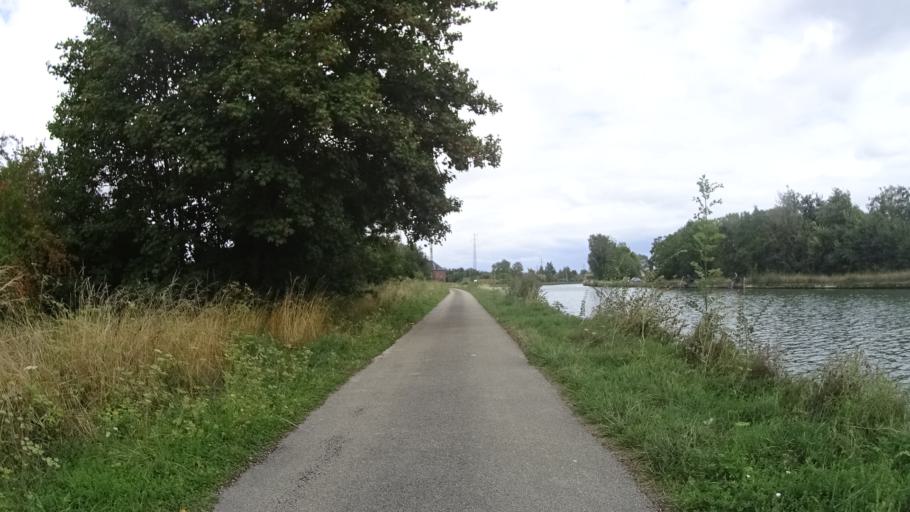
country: FR
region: Picardie
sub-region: Departement de l'Aisne
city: Tergnier
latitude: 49.6494
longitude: 3.3021
